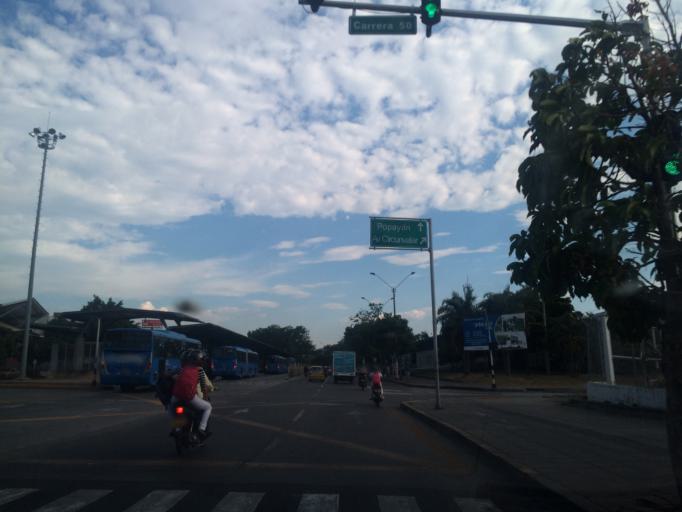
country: CO
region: Valle del Cauca
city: Cali
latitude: 3.4160
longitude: -76.5484
